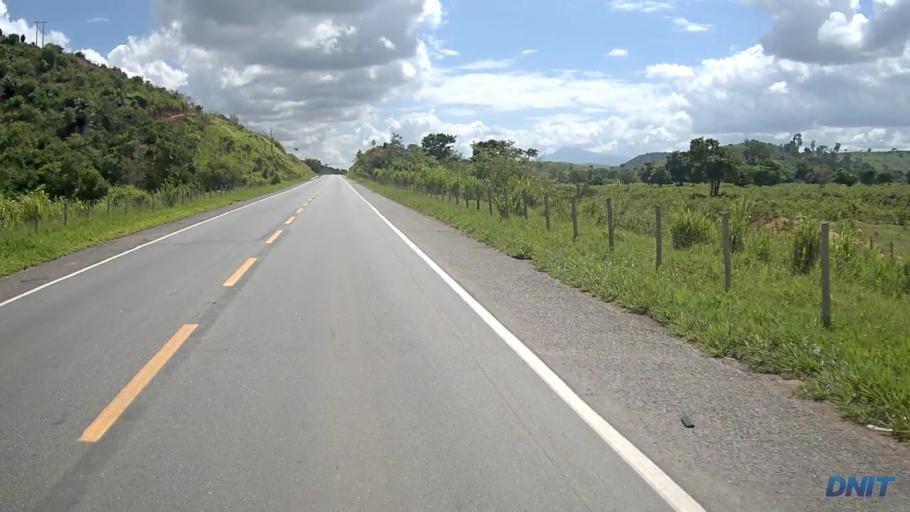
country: BR
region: Minas Gerais
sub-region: Governador Valadares
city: Governador Valadares
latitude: -18.9988
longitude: -42.1234
